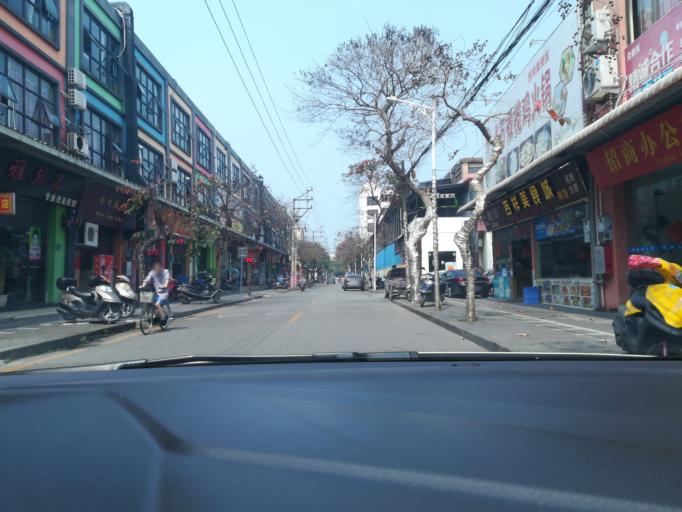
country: CN
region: Guangdong
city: Dagang
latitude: 22.8067
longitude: 113.4019
